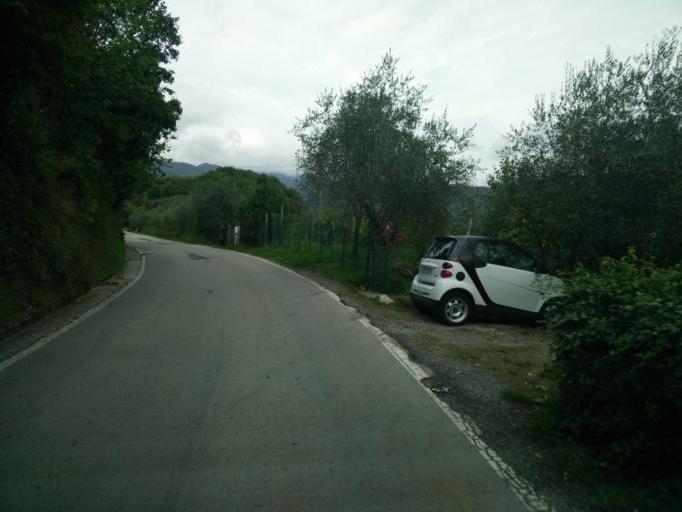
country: IT
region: Tuscany
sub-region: Provincia di Massa-Carrara
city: Casola in Lunigiana
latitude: 44.2120
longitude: 10.1868
